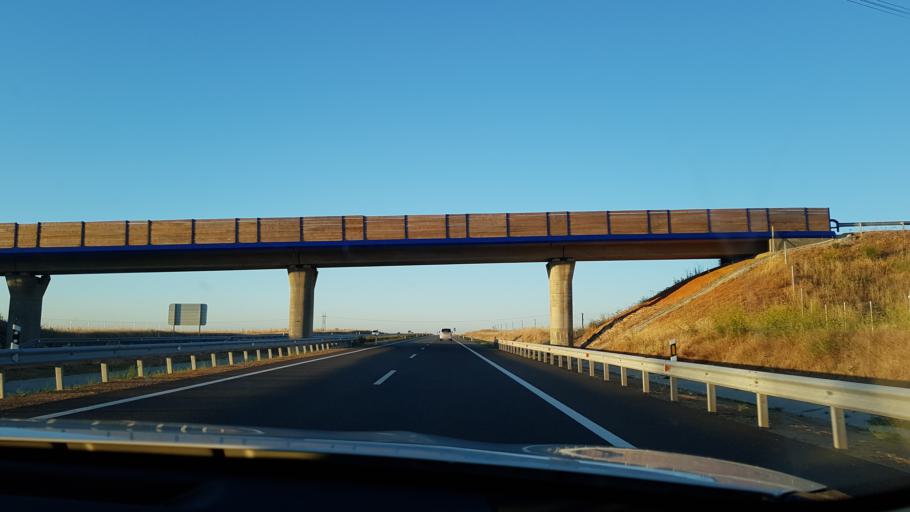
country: ES
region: Castille and Leon
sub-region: Provincia de Zamora
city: Montamarta
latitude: 41.6205
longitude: -5.7880
